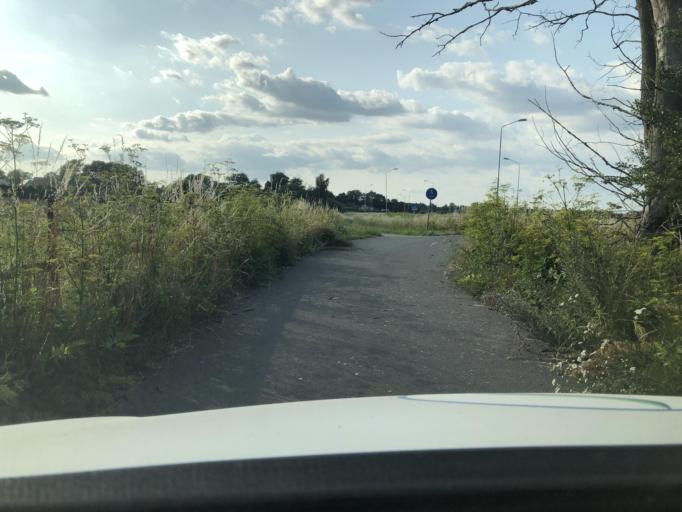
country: SE
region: Skane
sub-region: Kristianstads Kommun
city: Norra Asum
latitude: 55.9899
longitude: 14.1570
